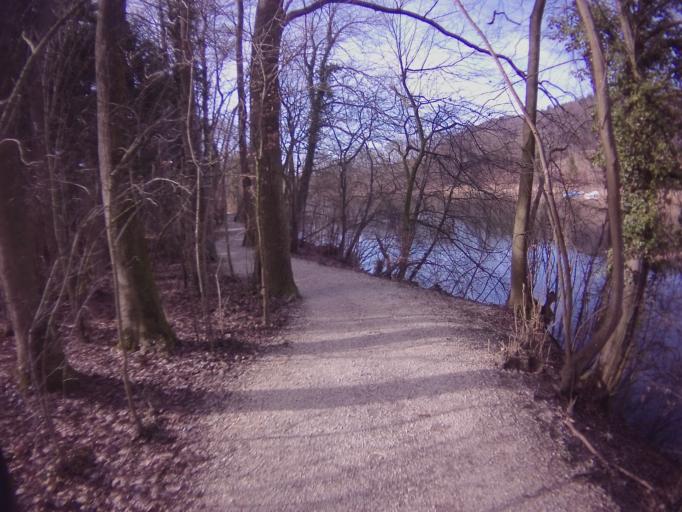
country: CH
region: Aargau
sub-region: Bezirk Baden
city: Spreitenbach
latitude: 47.4277
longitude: 8.3830
